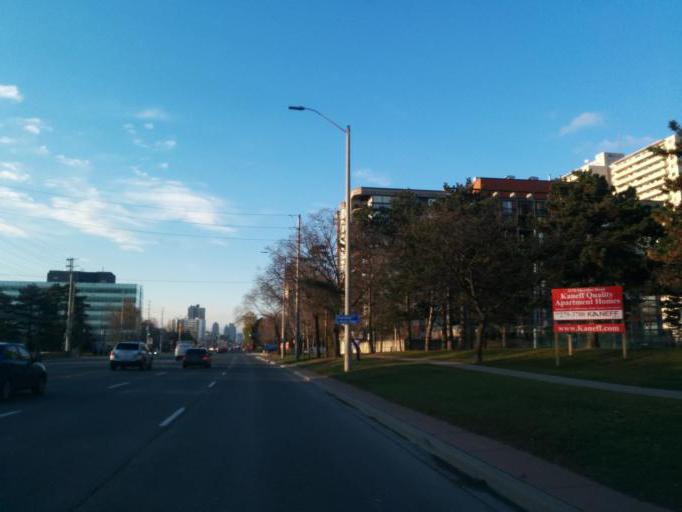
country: CA
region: Ontario
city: Mississauga
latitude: 43.5713
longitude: -79.6034
